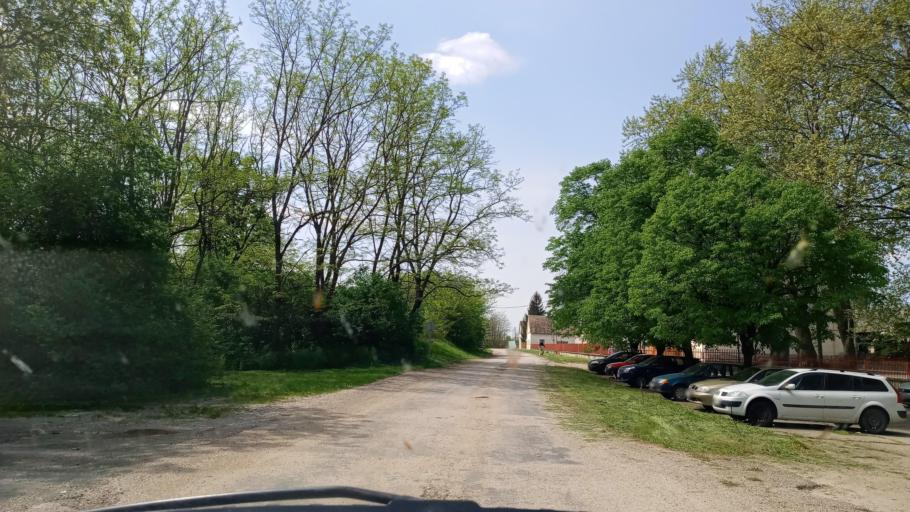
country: HU
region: Baranya
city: Boly
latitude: 45.9390
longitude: 18.5394
